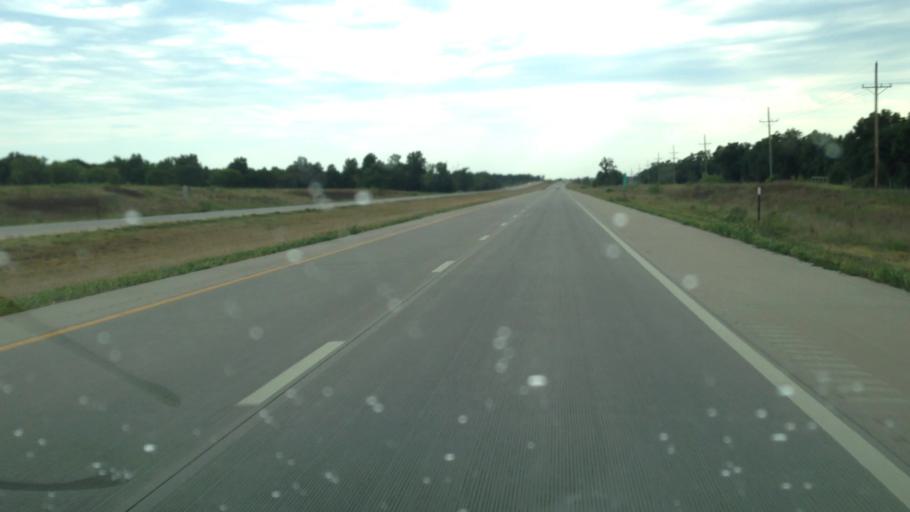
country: US
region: Kansas
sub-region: Douglas County
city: Baldwin City
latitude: 38.7496
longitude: -95.2679
